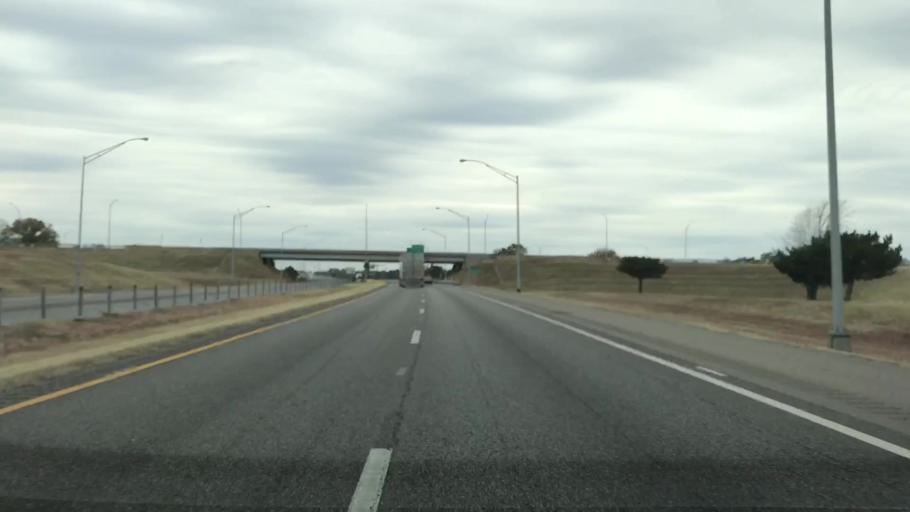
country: US
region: Oklahoma
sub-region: Custer County
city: Clinton
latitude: 35.5007
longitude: -98.9623
